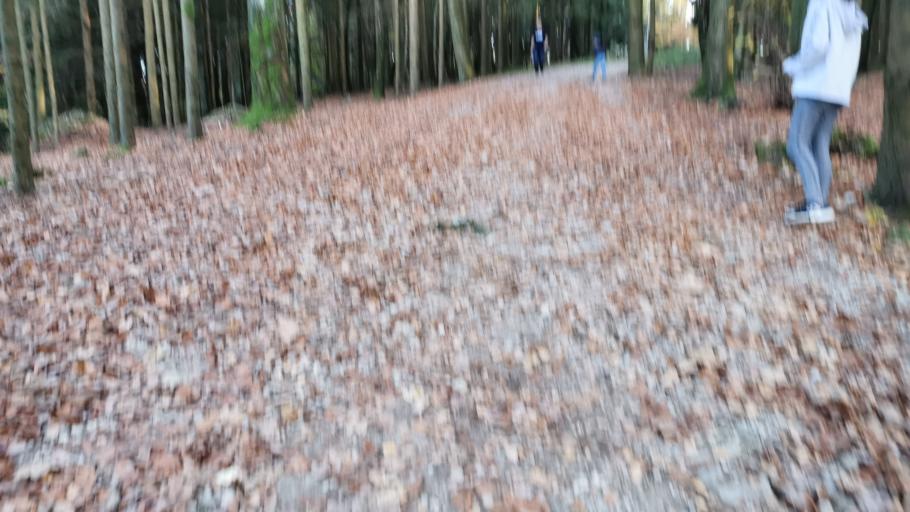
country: AT
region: Upper Austria
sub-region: Politischer Bezirk Vocklabruck
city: Redleiten
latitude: 48.0937
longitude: 13.5259
